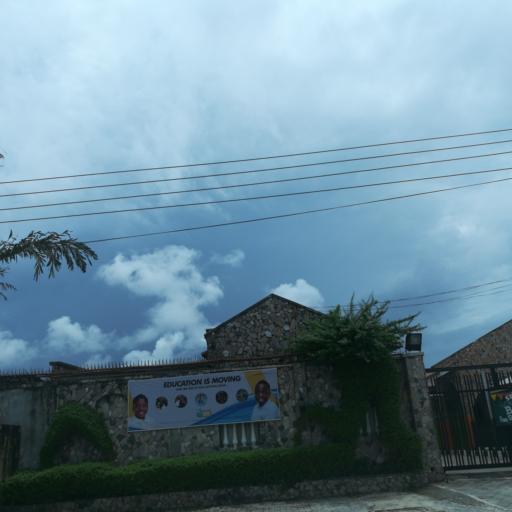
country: NG
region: Lagos
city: Ikoyi
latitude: 6.4457
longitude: 3.4623
